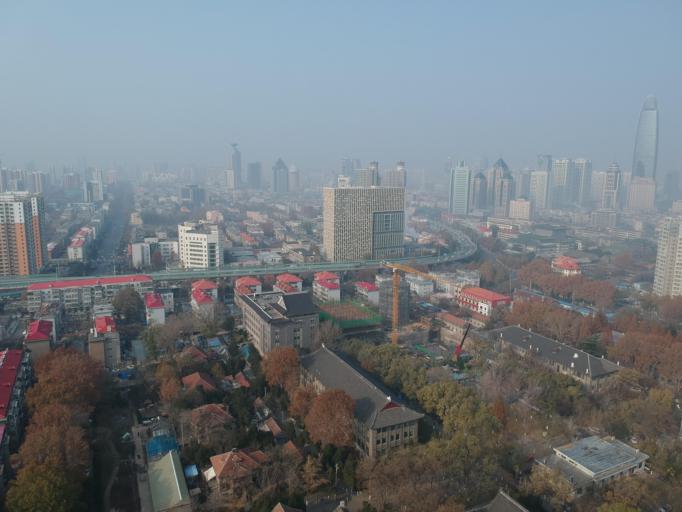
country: CN
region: Shandong Sheng
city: Jinan
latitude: 36.6517
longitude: 117.0119
